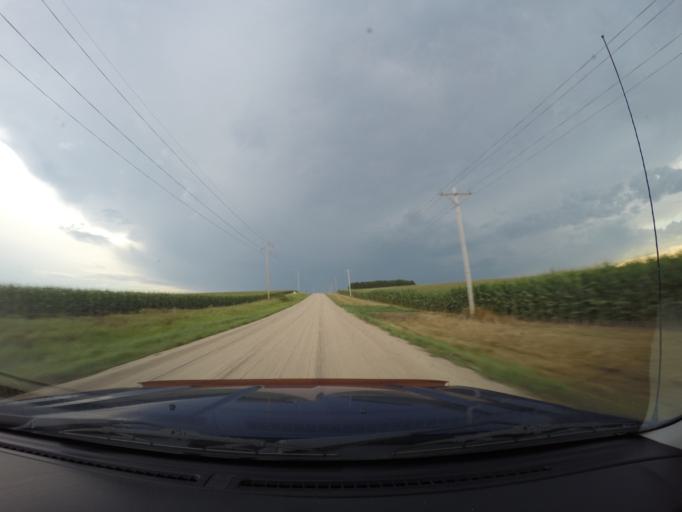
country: US
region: Nebraska
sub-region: Buffalo County
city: Kearney
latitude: 40.8436
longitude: -99.1574
